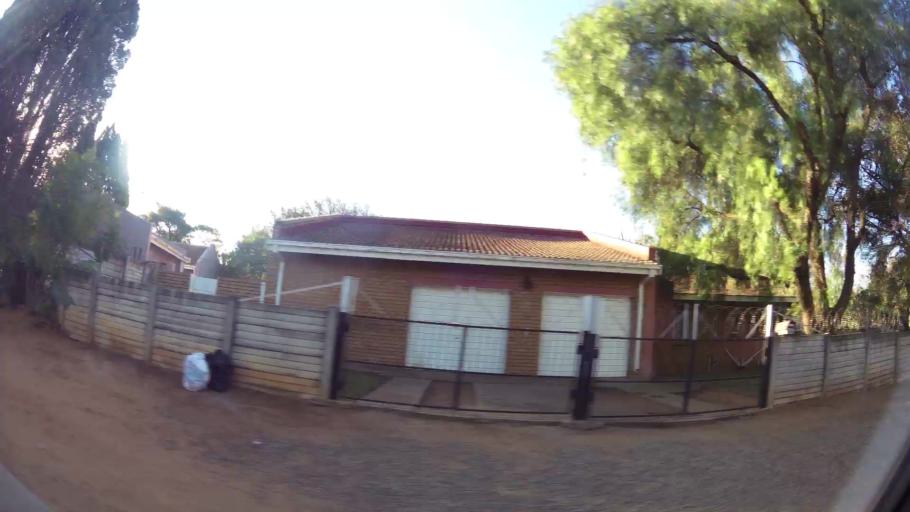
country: ZA
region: North-West
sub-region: Bojanala Platinum District Municipality
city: Rustenburg
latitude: -25.6743
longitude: 27.2084
